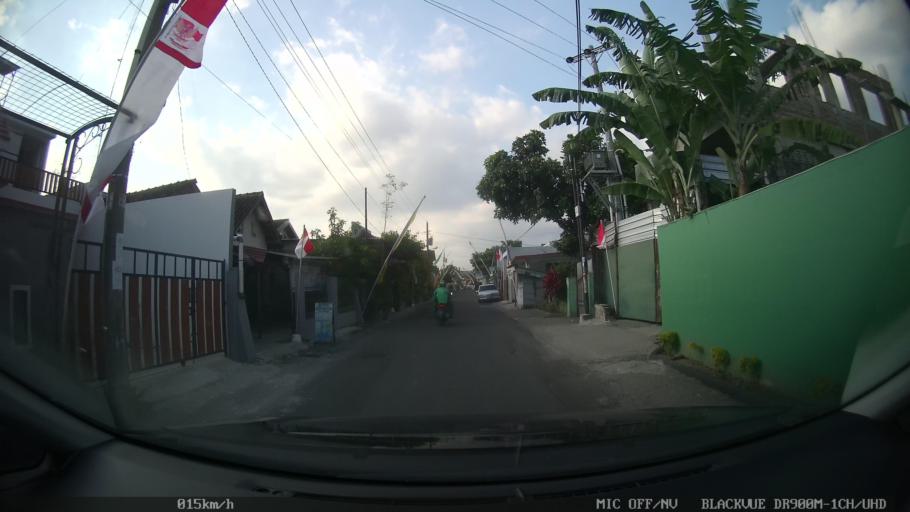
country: ID
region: Daerah Istimewa Yogyakarta
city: Yogyakarta
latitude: -7.7908
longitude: 110.3508
